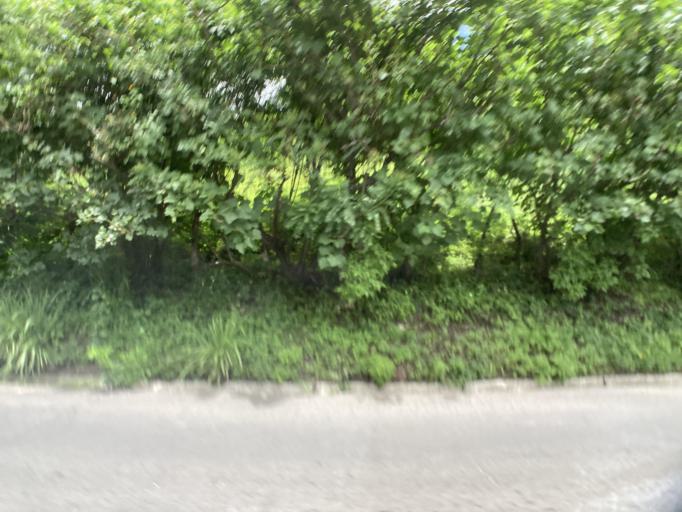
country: GT
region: Guatemala
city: Amatitlan
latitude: 14.4701
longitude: -90.5890
